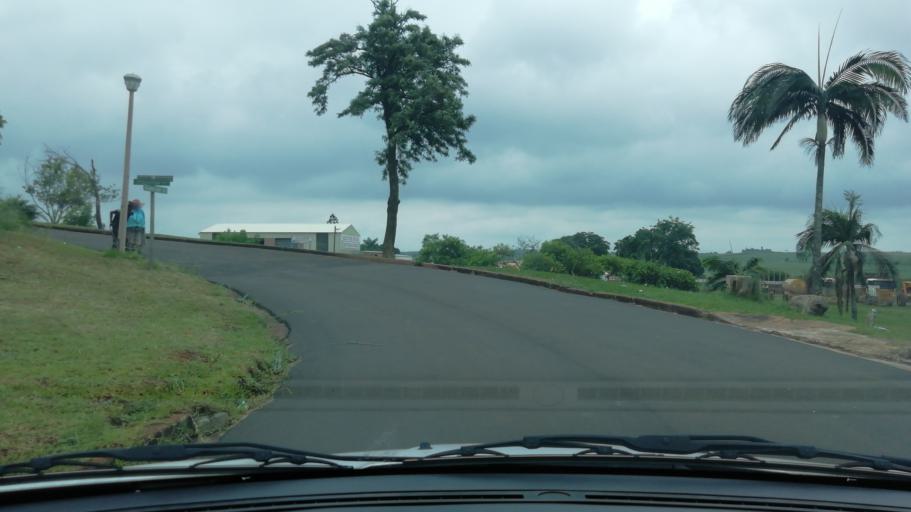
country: ZA
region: KwaZulu-Natal
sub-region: uThungulu District Municipality
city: Empangeni
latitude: -28.7624
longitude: 31.9049
